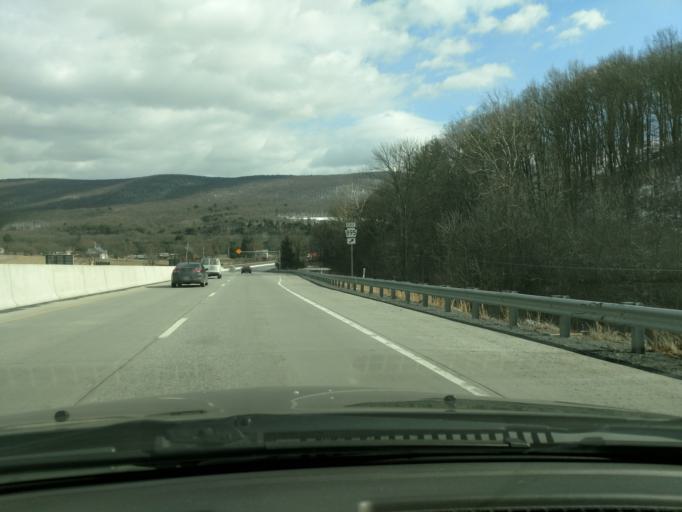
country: US
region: Pennsylvania
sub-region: Berks County
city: West Hamburg
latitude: 40.6128
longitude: -76.0355
